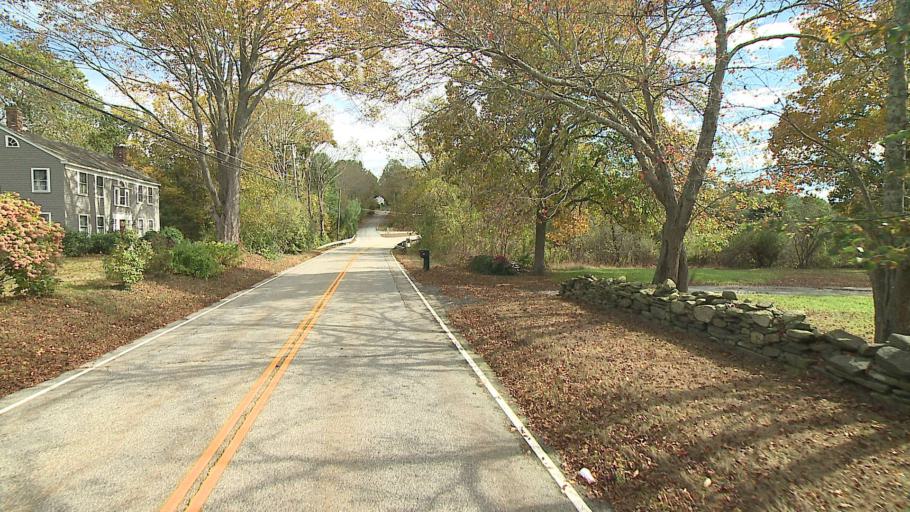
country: US
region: Connecticut
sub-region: Windham County
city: Putnam
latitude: 41.8955
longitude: -71.8807
